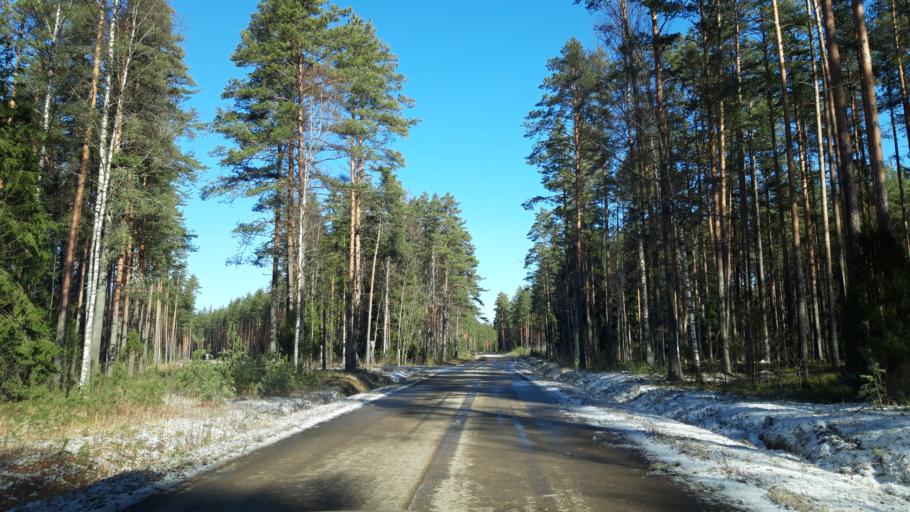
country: LV
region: Strenci
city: Strenci
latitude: 57.5782
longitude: 25.7117
